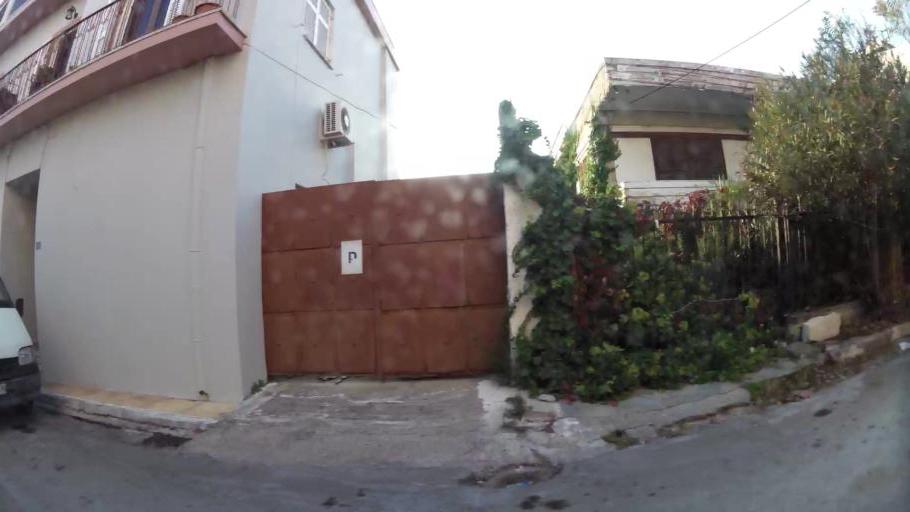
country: GR
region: Attica
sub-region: Nomarchia Anatolikis Attikis
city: Acharnes
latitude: 38.0855
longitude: 23.7346
